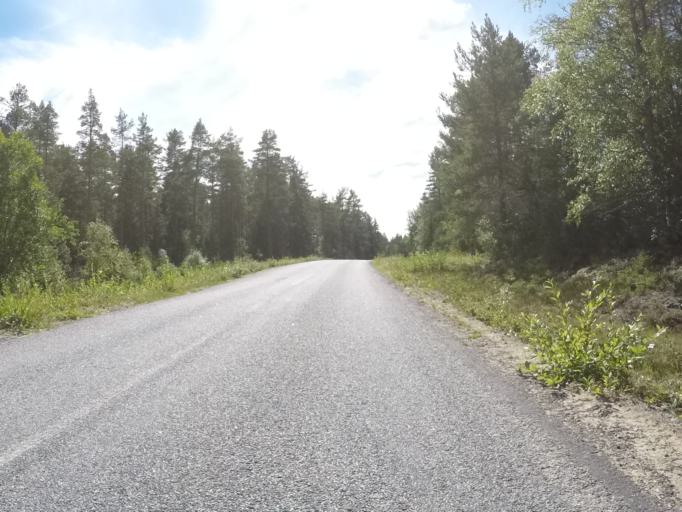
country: SE
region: Vaesterbotten
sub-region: Umea Kommun
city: Saevar
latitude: 63.9404
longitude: 20.7870
